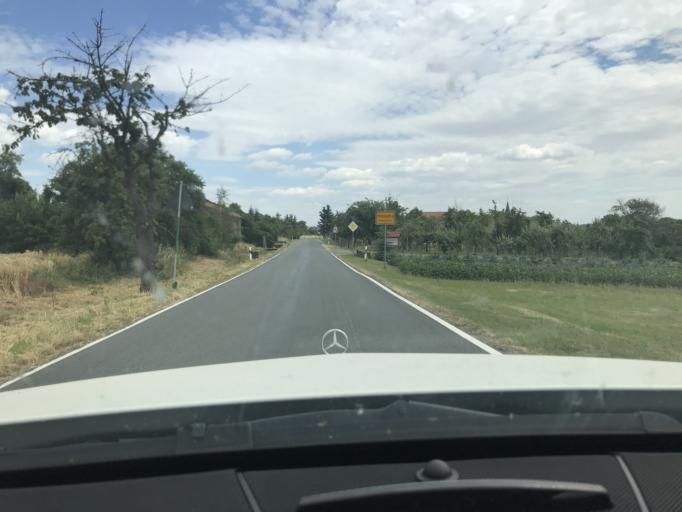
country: DE
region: Thuringia
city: Holzsussra
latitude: 51.2948
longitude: 10.6892
